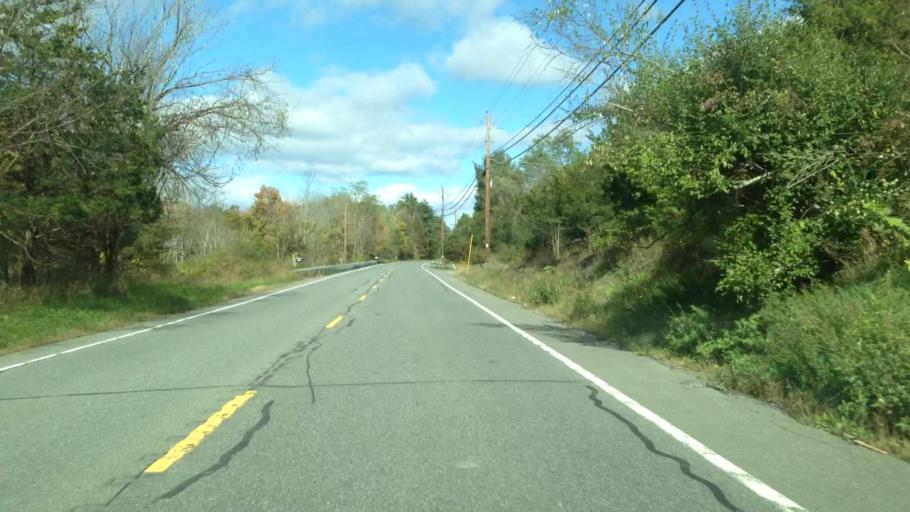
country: US
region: New York
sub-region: Ulster County
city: New Paltz
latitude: 41.7717
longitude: -74.0758
